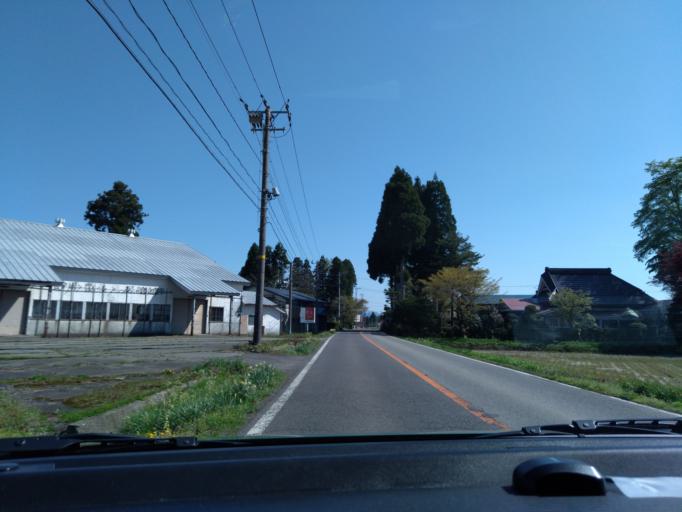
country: JP
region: Akita
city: Kakunodatemachi
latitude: 39.5663
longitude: 140.5831
